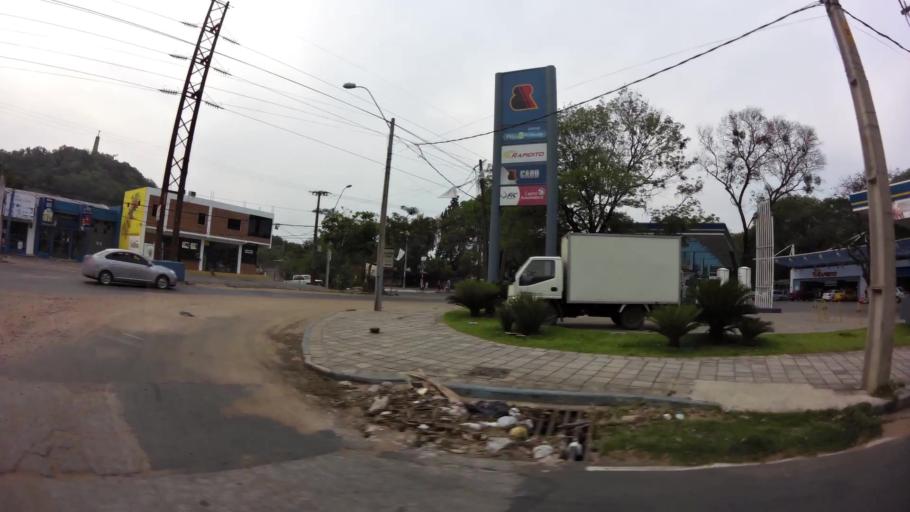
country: PY
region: Central
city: Lambare
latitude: -25.3429
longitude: -57.6376
